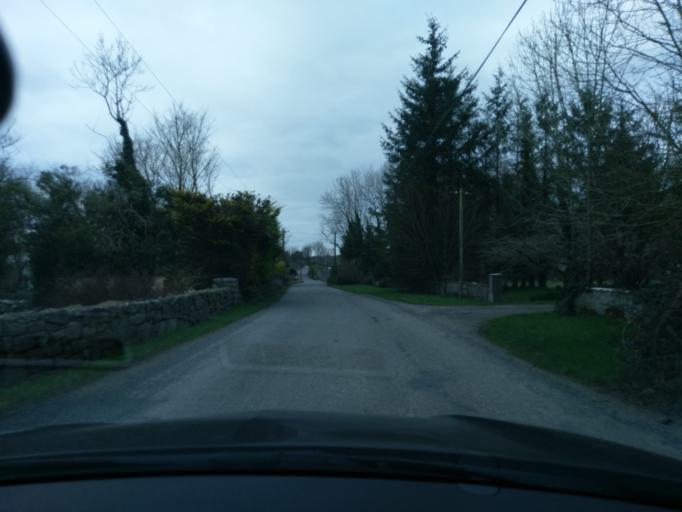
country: IE
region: Connaught
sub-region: County Galway
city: Oranmore
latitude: 53.2182
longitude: -8.8379
